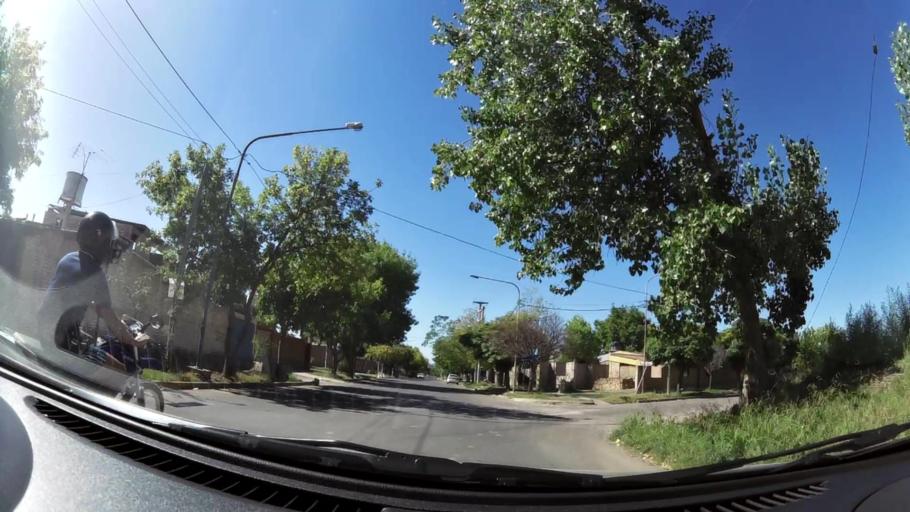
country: AR
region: Mendoza
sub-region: Departamento de Godoy Cruz
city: Godoy Cruz
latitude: -32.9523
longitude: -68.8222
